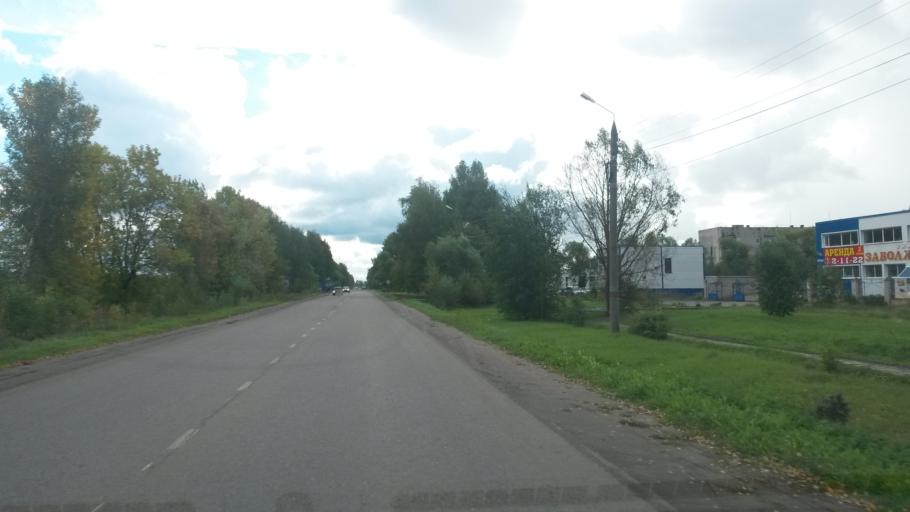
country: RU
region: Ivanovo
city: Zavolzhsk
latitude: 57.4764
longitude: 42.1532
